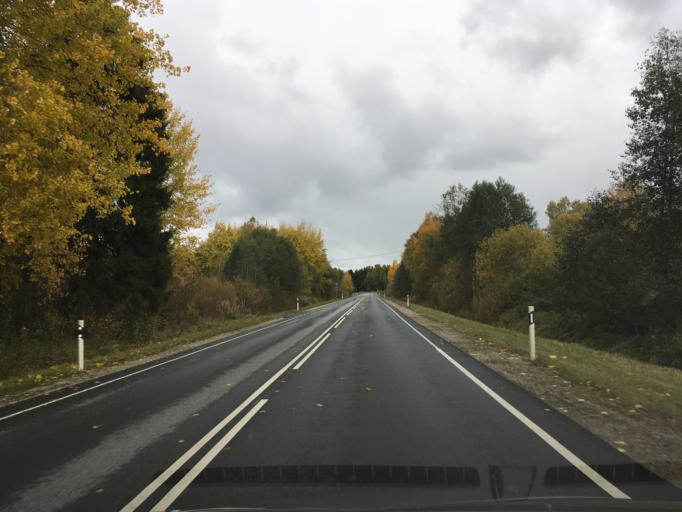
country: EE
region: Harju
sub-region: Anija vald
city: Kehra
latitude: 59.3138
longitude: 25.3435
